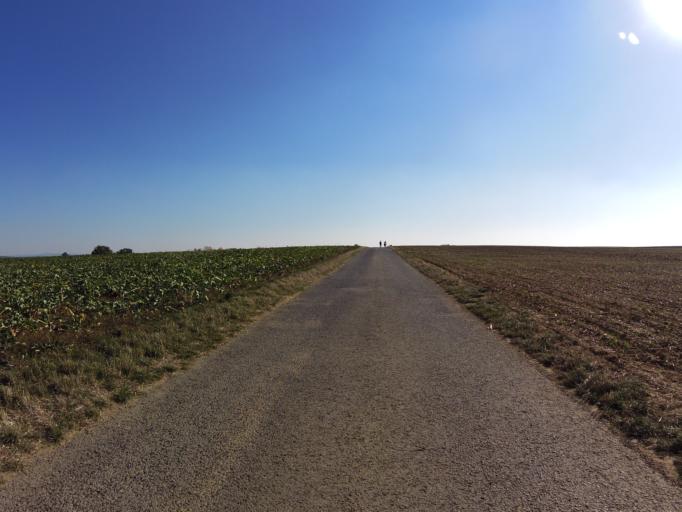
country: DE
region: Bavaria
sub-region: Regierungsbezirk Unterfranken
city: Eibelstadt
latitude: 49.7212
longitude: 9.9777
